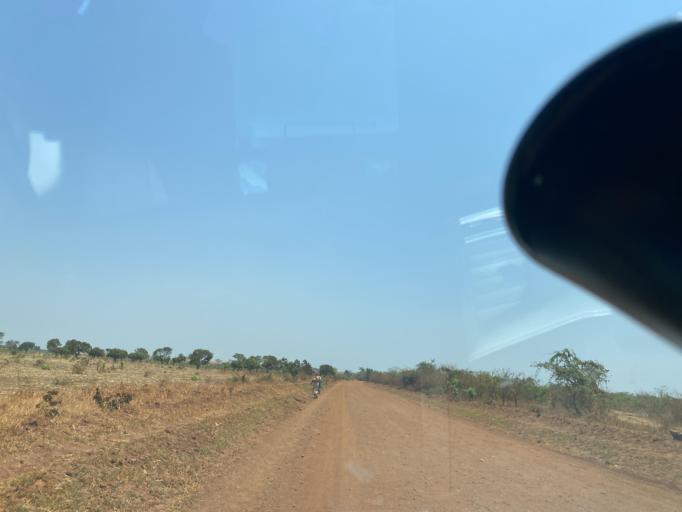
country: ZM
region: Southern
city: Nakambala
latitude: -15.5005
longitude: 27.9119
